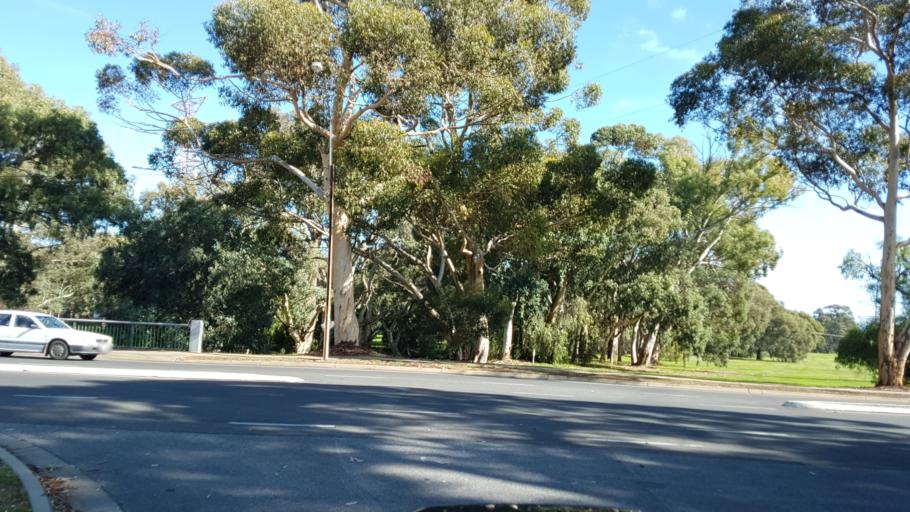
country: AU
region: South Australia
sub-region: Salisbury
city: Salisbury
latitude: -34.7582
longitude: 138.6350
